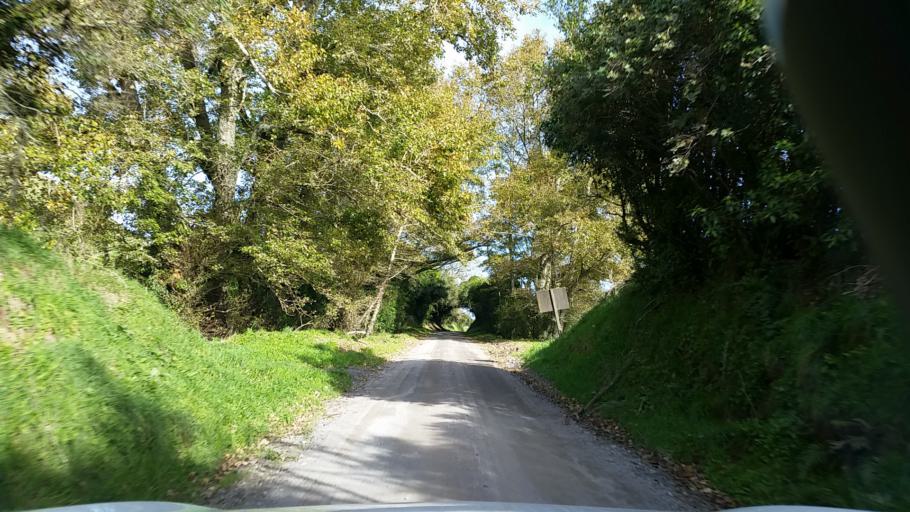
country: NZ
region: Bay of Plenty
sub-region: Rotorua District
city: Rotorua
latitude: -38.2419
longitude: 176.3454
